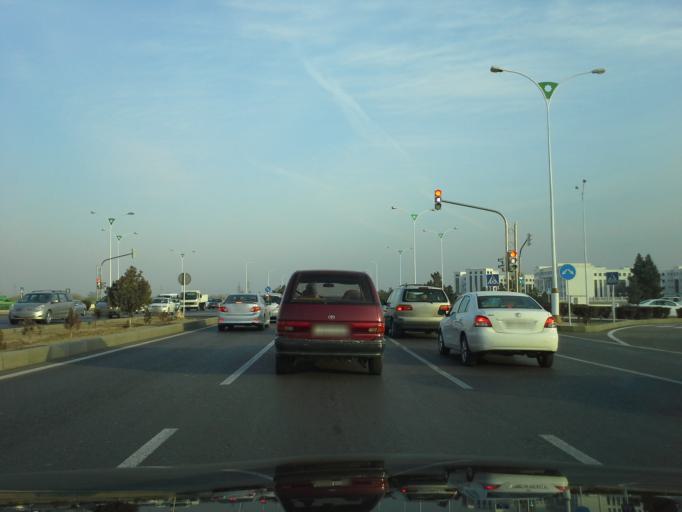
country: TM
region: Ahal
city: Abadan
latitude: 38.0465
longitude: 58.1994
